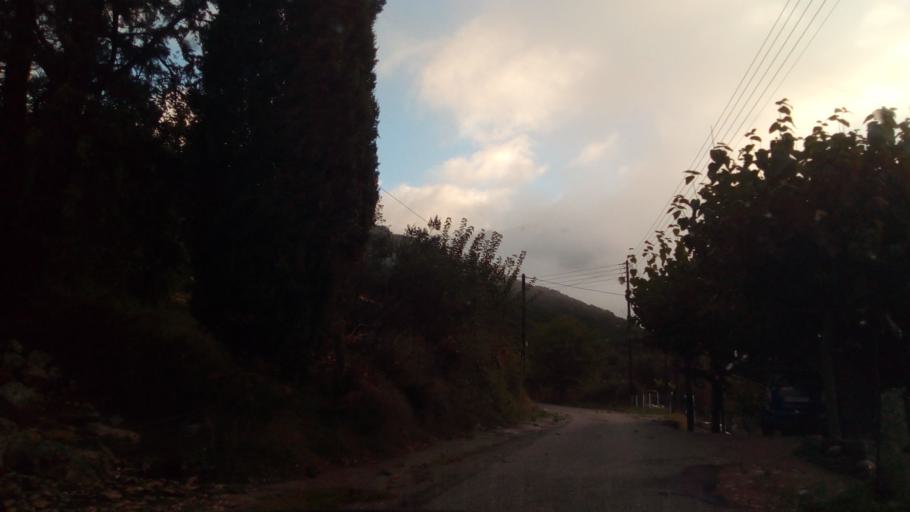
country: GR
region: West Greece
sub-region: Nomos Aitolias kai Akarnanias
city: Thermo
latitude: 38.5186
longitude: 21.7676
